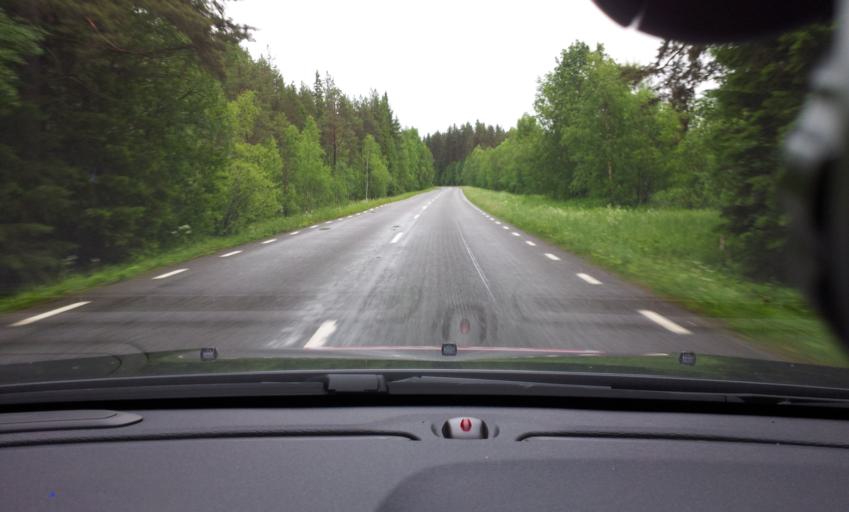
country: SE
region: Jaemtland
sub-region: Stroemsunds Kommun
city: Stroemsund
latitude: 63.4306
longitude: 15.5000
